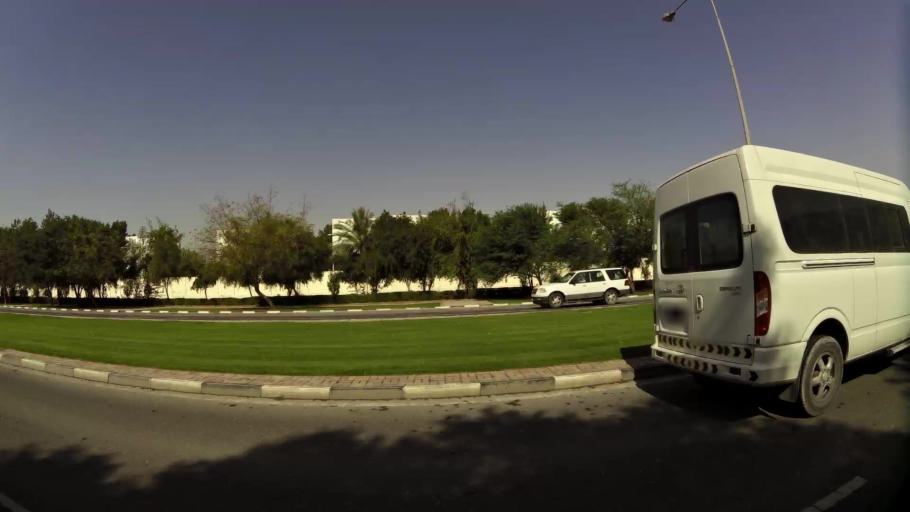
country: QA
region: Baladiyat ad Dawhah
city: Doha
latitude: 25.3251
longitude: 51.5168
